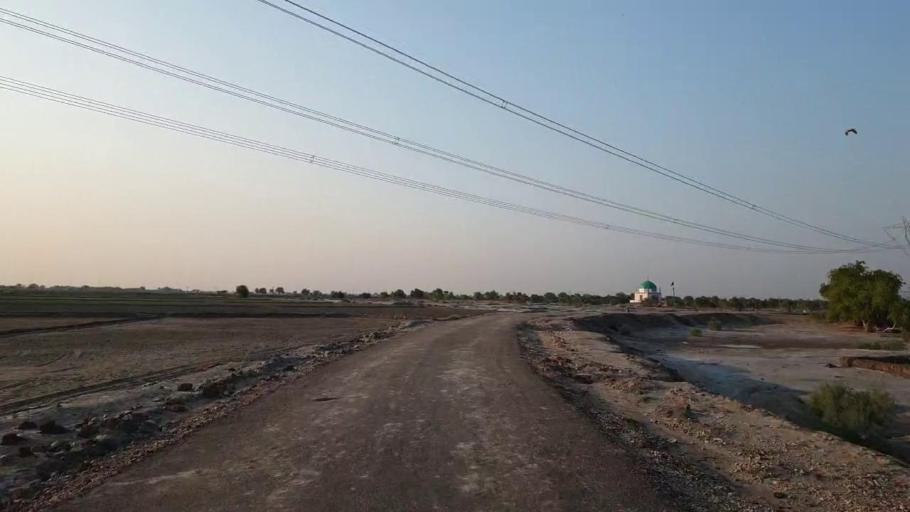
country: PK
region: Sindh
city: Sehwan
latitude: 26.4324
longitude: 67.7646
